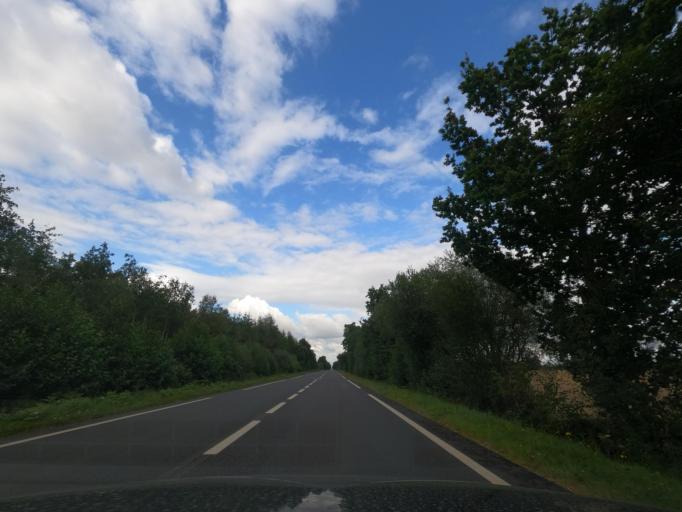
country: FR
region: Lower Normandy
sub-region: Departement du Calvados
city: Orbec
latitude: 48.8958
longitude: 0.4037
